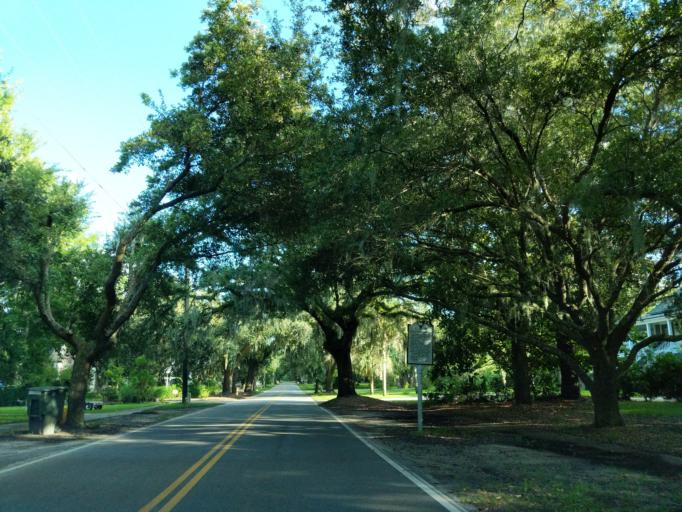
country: US
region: South Carolina
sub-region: Charleston County
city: Awendaw
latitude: 33.0838
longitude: -79.4598
